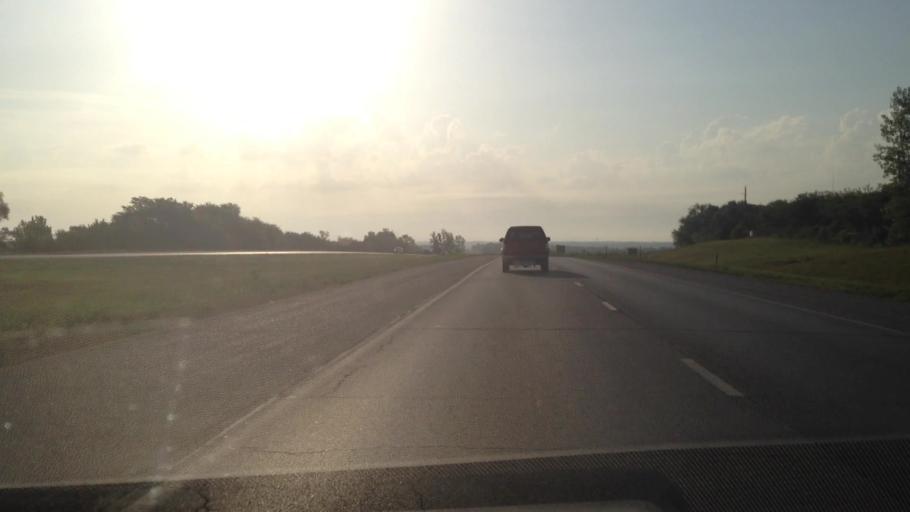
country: US
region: Kansas
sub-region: Douglas County
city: Lawrence
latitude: 38.9421
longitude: -95.1870
